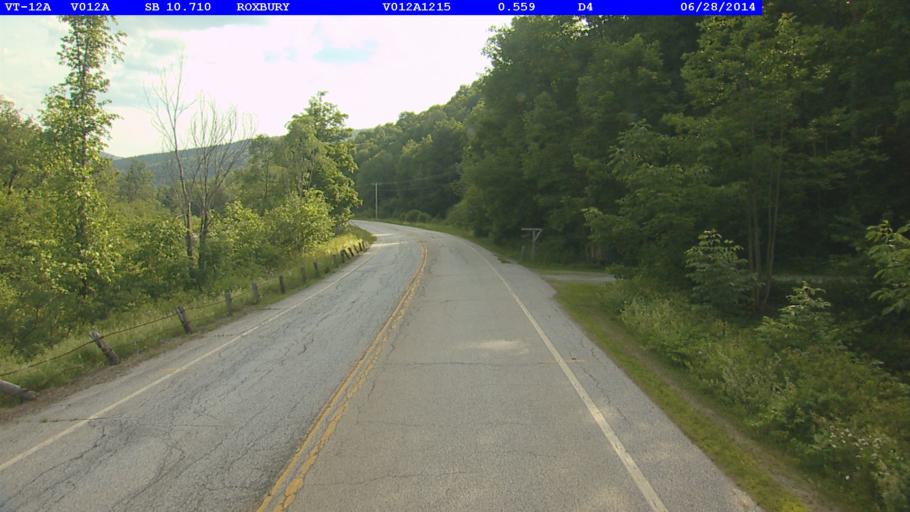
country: US
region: Vermont
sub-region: Orange County
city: Randolph
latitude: 44.0402
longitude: -72.7499
